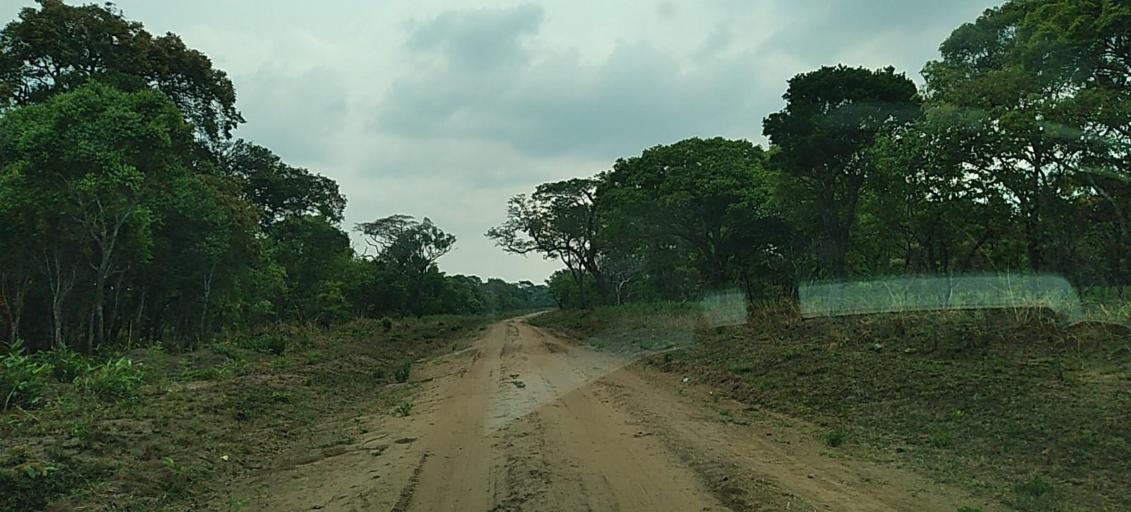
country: ZM
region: North-Western
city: Mwinilunga
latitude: -11.4132
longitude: 24.6133
